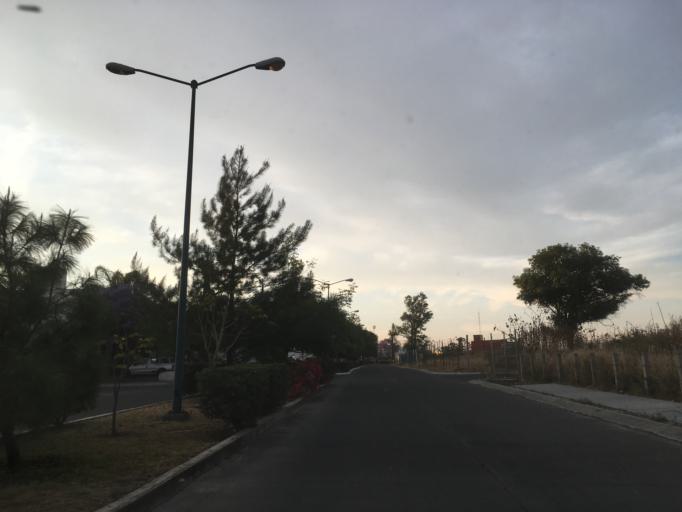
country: MX
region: Michoacan
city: Morelia
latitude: 19.6850
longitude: -101.2096
